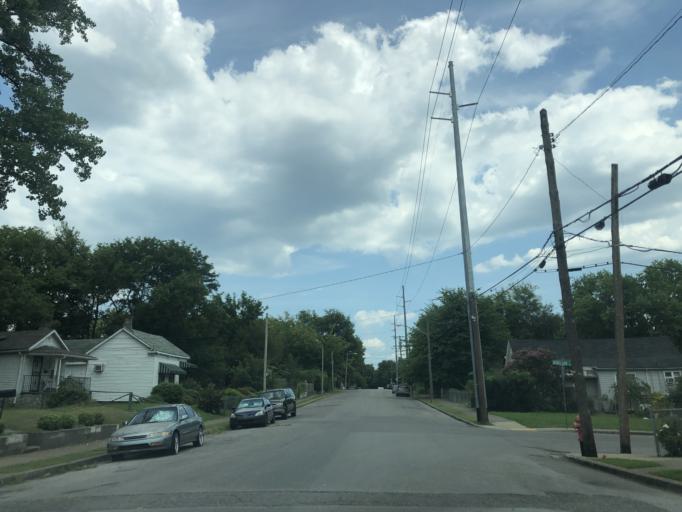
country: US
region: Tennessee
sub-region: Davidson County
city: Nashville
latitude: 36.1515
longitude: -86.7555
